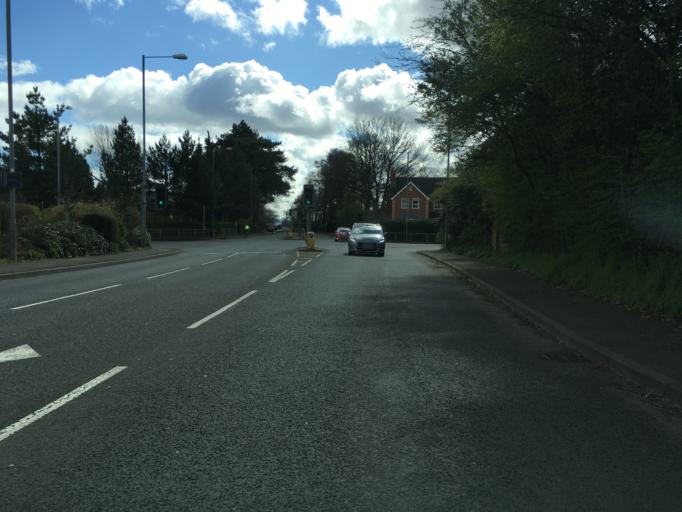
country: GB
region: Wales
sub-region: Monmouthshire
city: Chepstow
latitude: 51.6402
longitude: -2.6882
